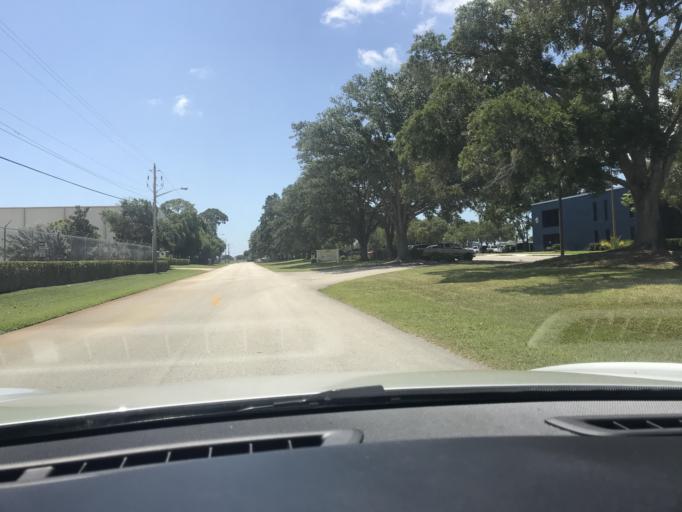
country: US
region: Florida
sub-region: Indian River County
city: Gifford
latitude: 27.6552
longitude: -80.4296
